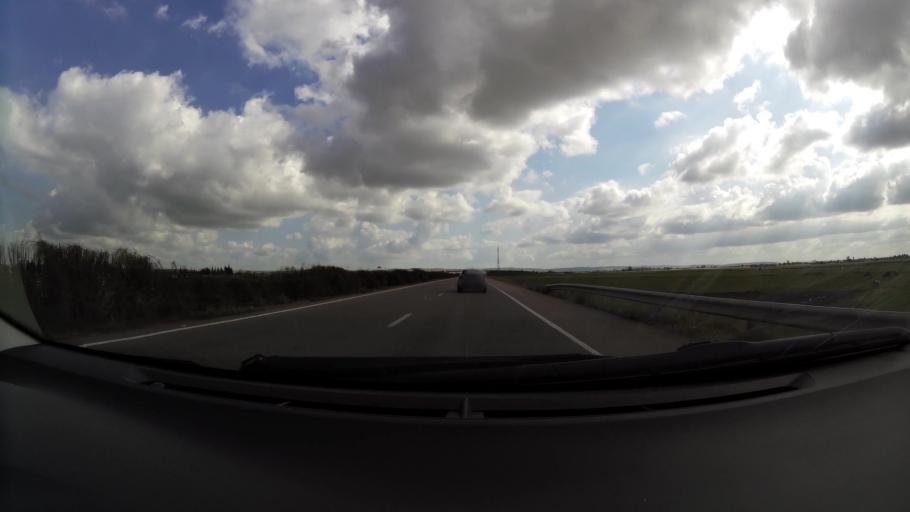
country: MA
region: Chaouia-Ouardigha
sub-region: Settat Province
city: Berrechid
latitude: 33.1414
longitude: -7.5753
